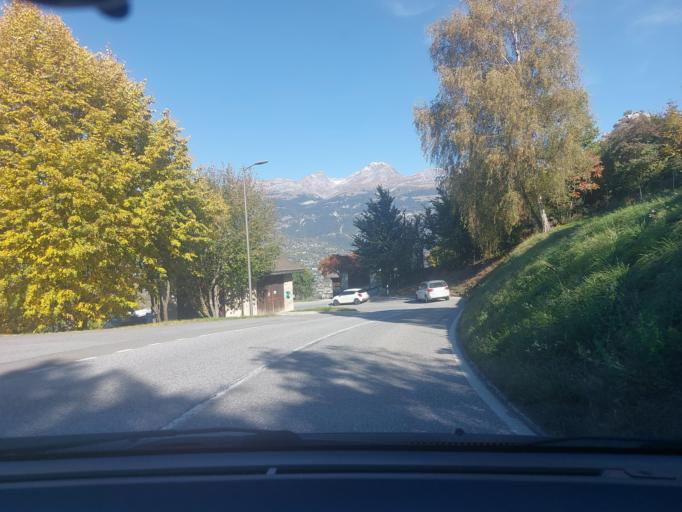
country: CH
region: Valais
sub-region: Sierre District
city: Chippis
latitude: 46.2730
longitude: 7.5510
